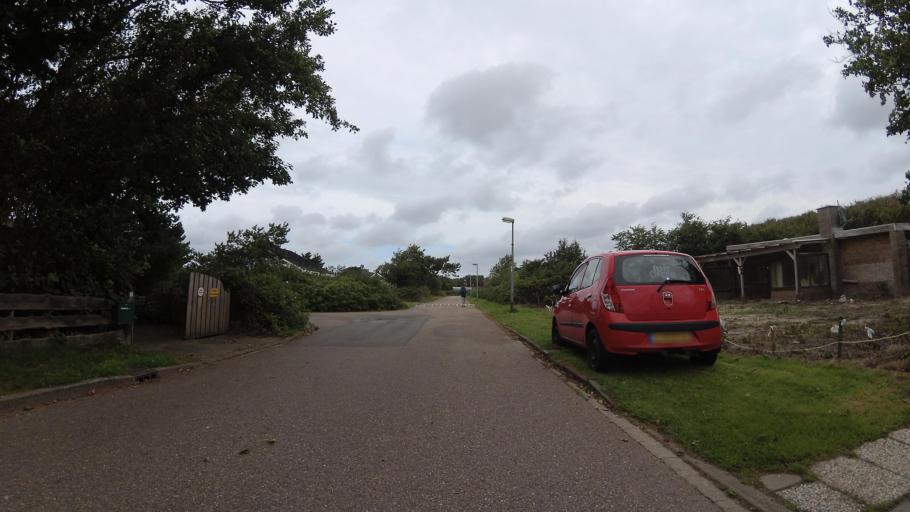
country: NL
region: North Holland
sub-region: Gemeente Den Helder
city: Den Helder
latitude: 52.9014
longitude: 4.7210
